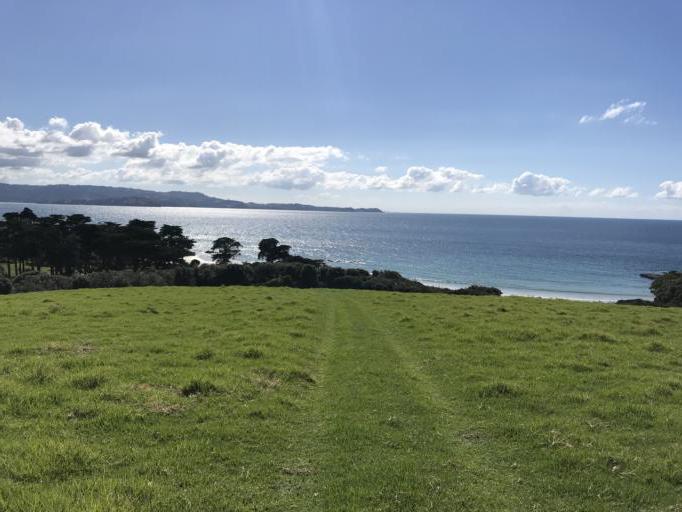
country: NZ
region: Auckland
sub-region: Auckland
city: Warkworth
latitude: -36.3708
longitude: 174.8354
